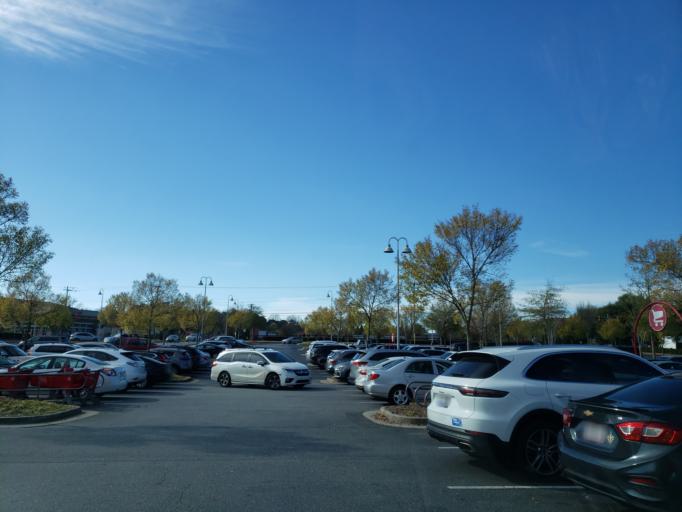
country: US
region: Georgia
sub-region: Fulton County
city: Alpharetta
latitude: 34.0993
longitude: -84.2694
